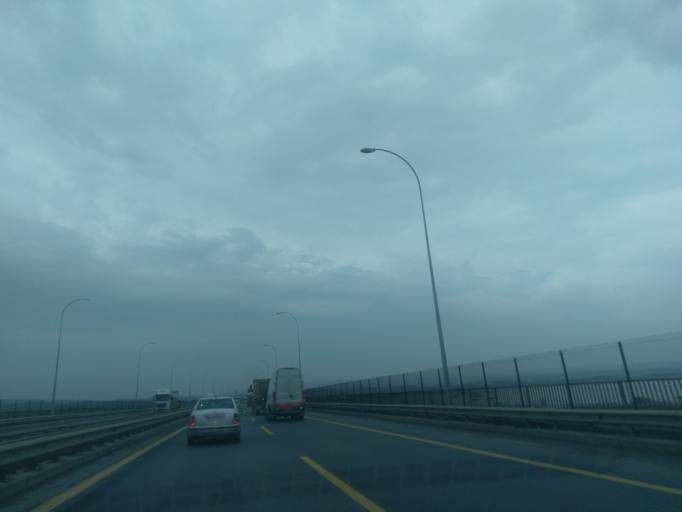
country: TR
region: Istanbul
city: Muratbey
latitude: 41.1024
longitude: 28.5247
